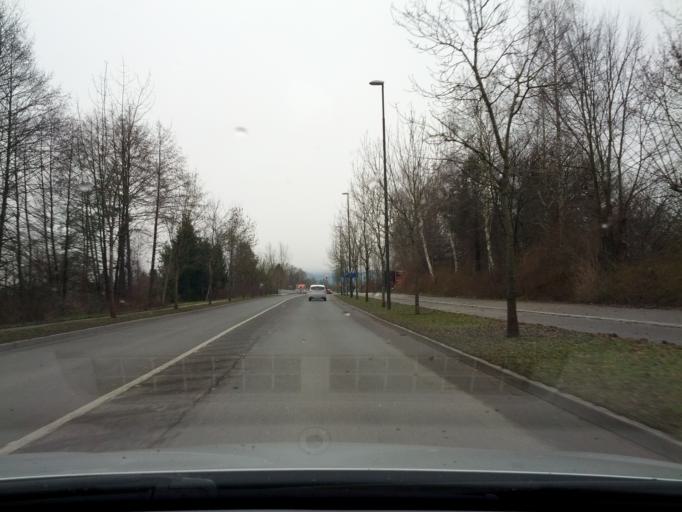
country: SI
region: Ljubljana
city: Ljubljana
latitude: 46.0347
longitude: 14.5002
